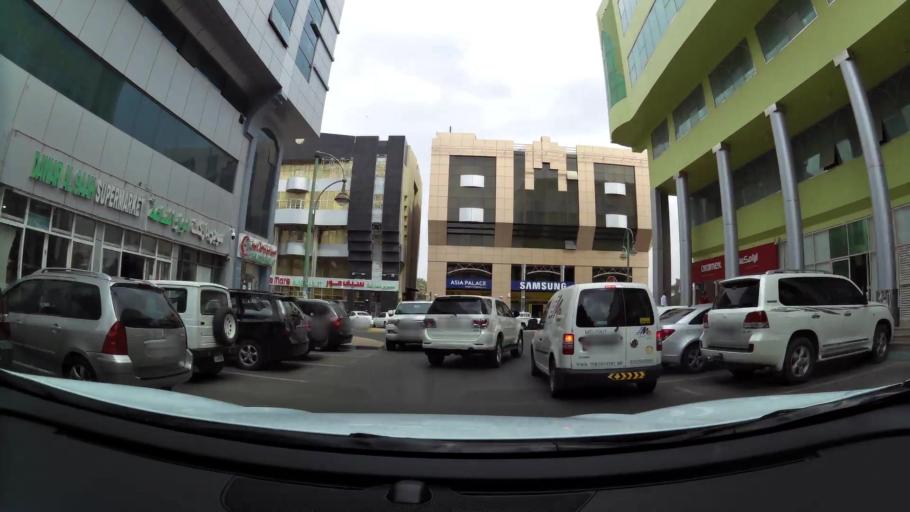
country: OM
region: Al Buraimi
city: Al Buraymi
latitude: 24.2228
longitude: 55.7742
